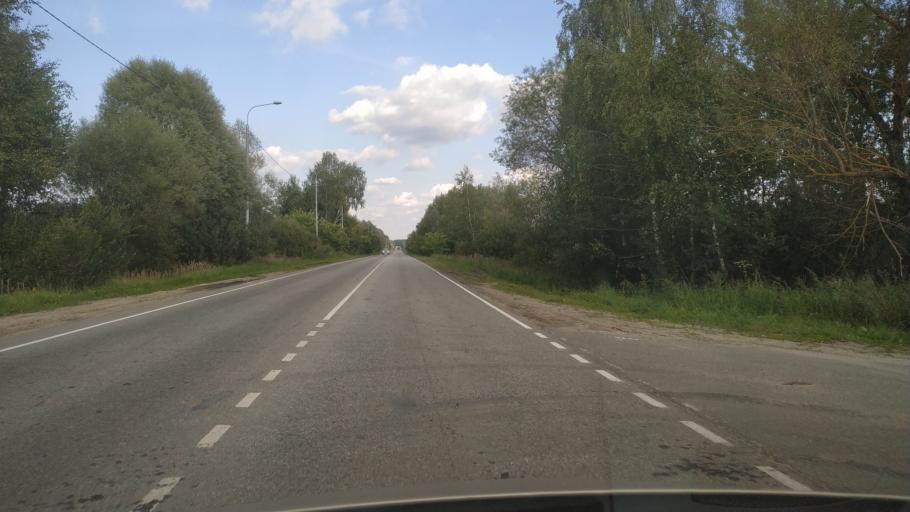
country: RU
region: Moskovskaya
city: Vereya
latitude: 55.7081
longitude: 39.1126
